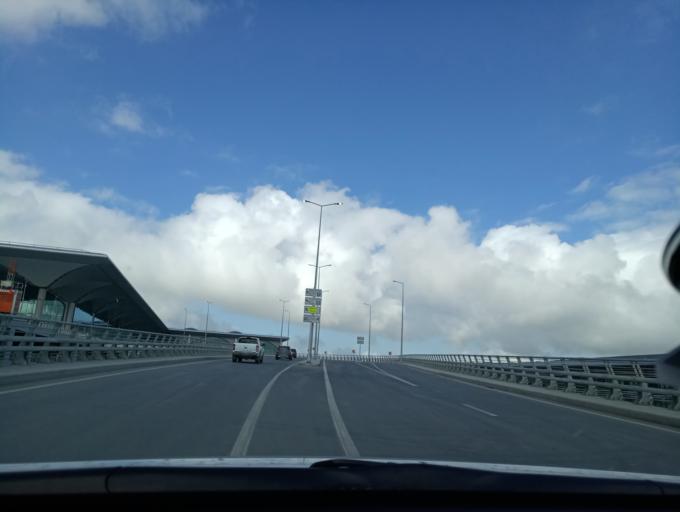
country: TR
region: Istanbul
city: Durusu
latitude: 41.2575
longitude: 28.7464
